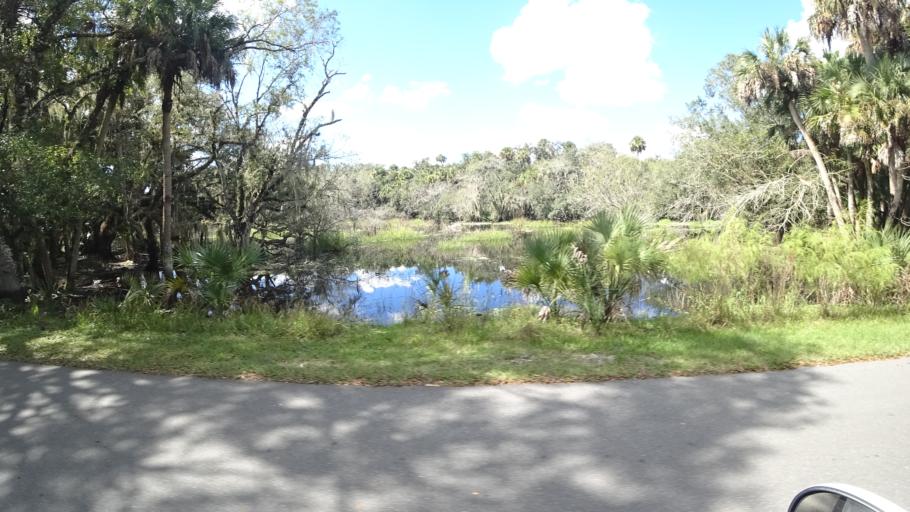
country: US
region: Florida
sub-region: Sarasota County
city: Lake Sarasota
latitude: 27.2626
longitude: -82.2862
